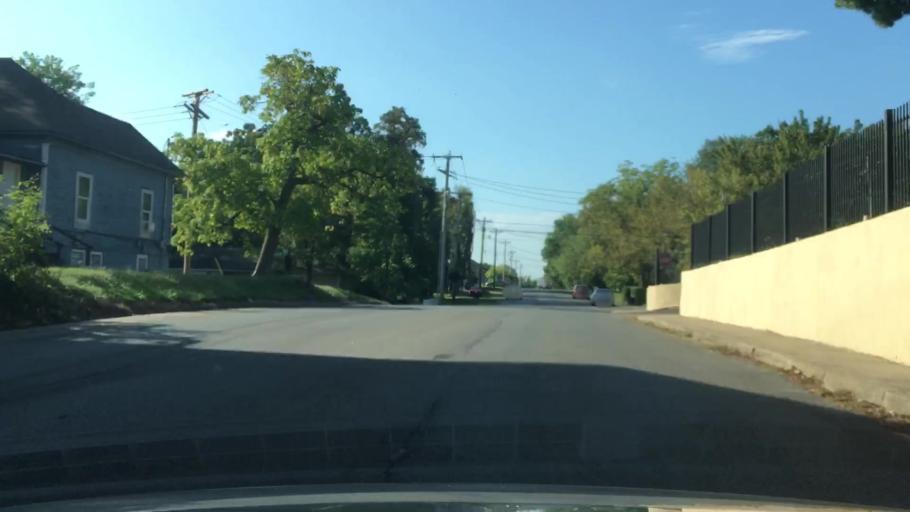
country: US
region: Oklahoma
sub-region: Cherokee County
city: Tahlequah
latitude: 35.9176
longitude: -94.9705
